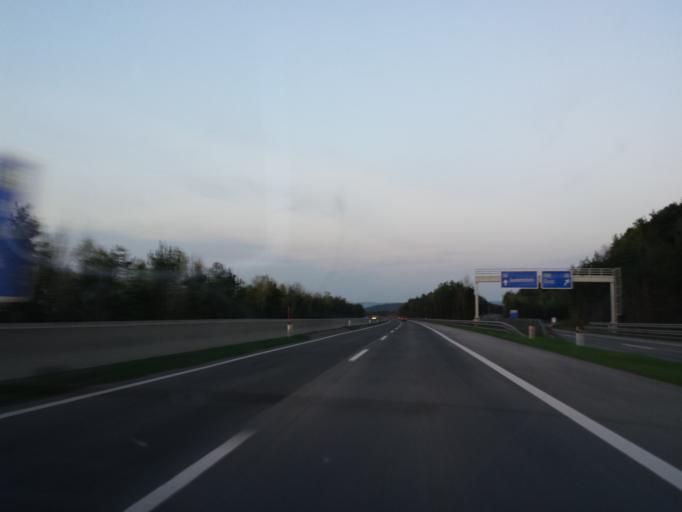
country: AT
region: Lower Austria
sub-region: Politischer Bezirk Neunkirchen
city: Seebenstein
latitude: 47.7110
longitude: 16.1179
